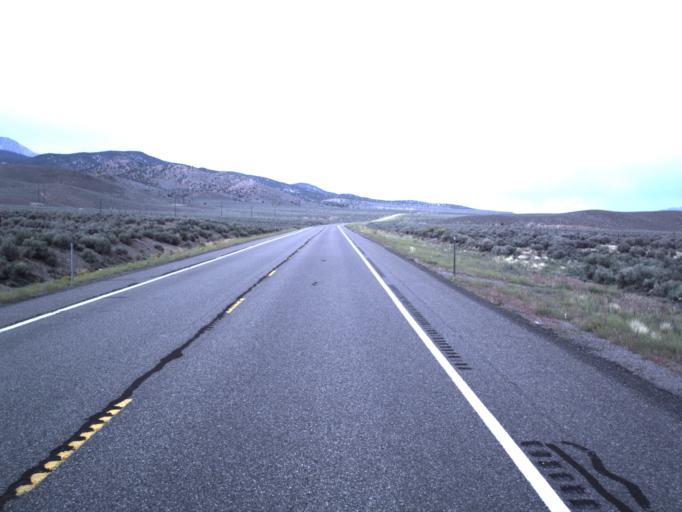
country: US
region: Utah
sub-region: Piute County
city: Junction
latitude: 38.2807
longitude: -112.2243
